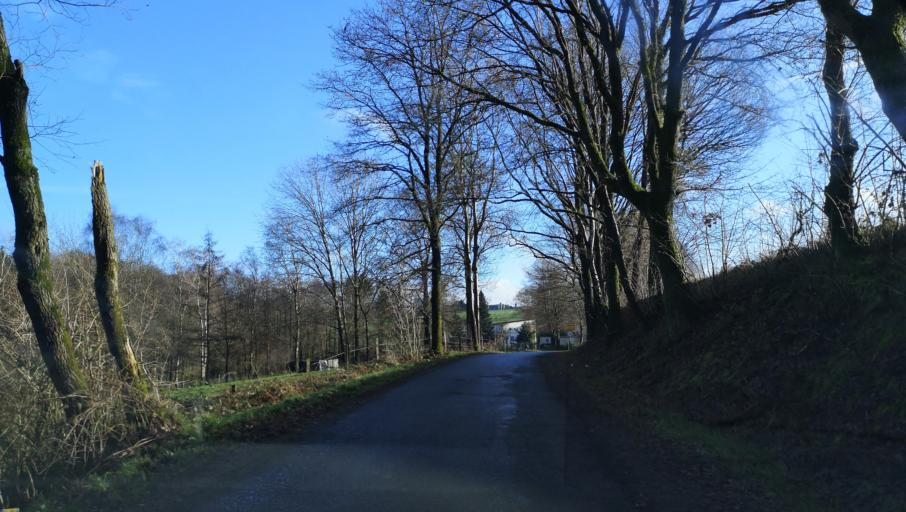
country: DE
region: North Rhine-Westphalia
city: Halver
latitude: 51.1849
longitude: 7.4316
